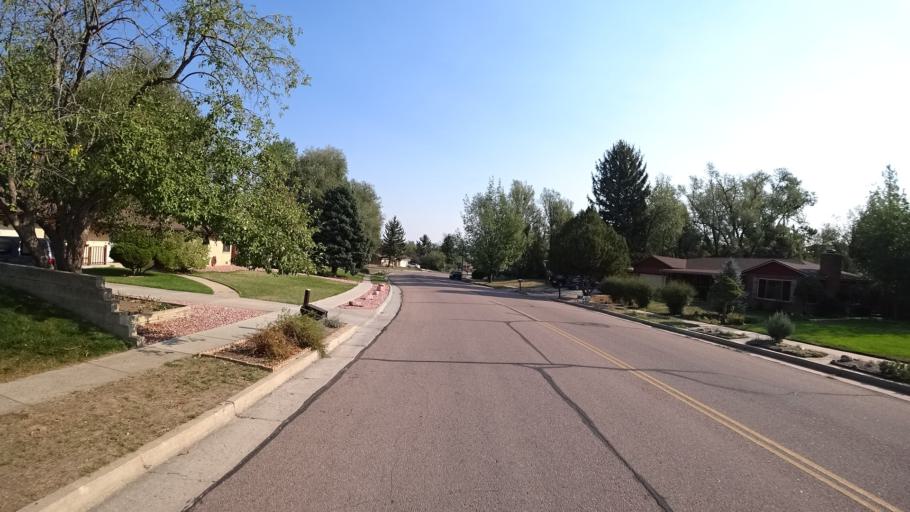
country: US
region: Colorado
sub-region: El Paso County
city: Colorado Springs
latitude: 38.8047
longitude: -104.8475
